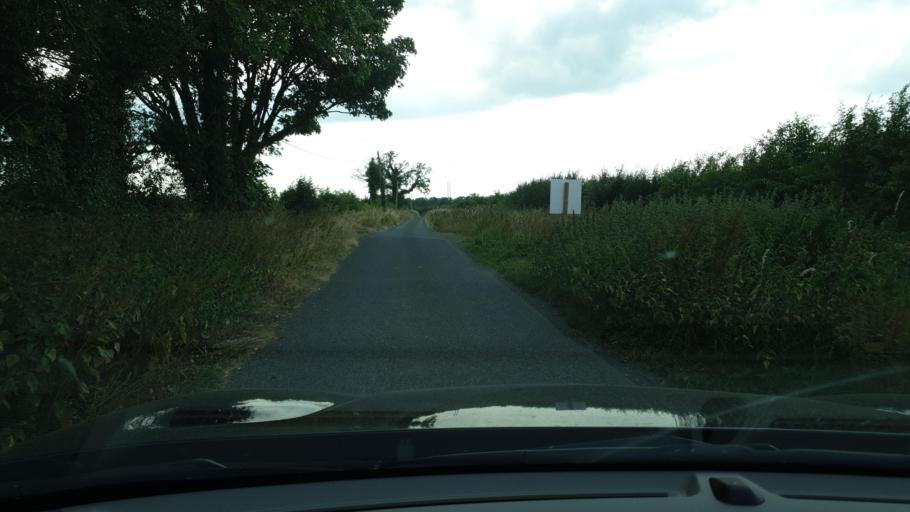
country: IE
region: Leinster
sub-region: An Mhi
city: Ashbourne
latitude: 53.4650
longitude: -6.4235
